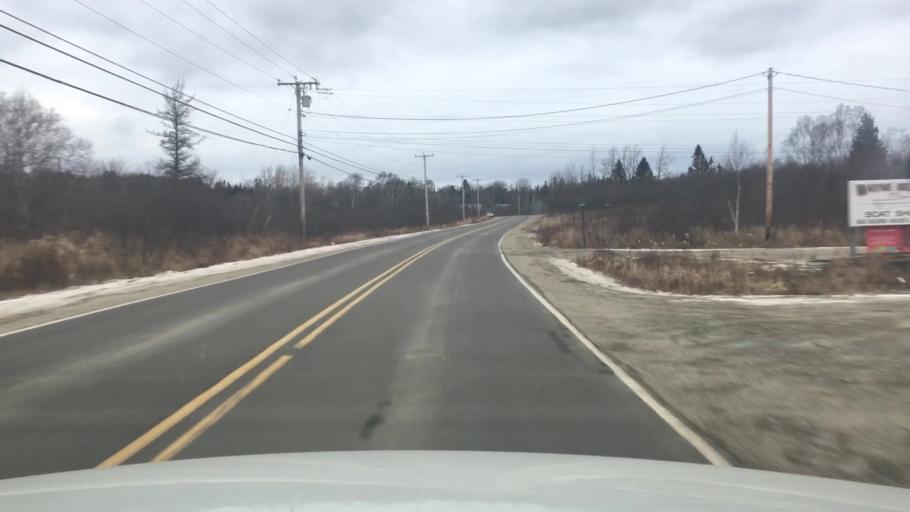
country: US
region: Maine
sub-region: Washington County
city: Jonesport
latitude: 44.5544
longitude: -67.6255
